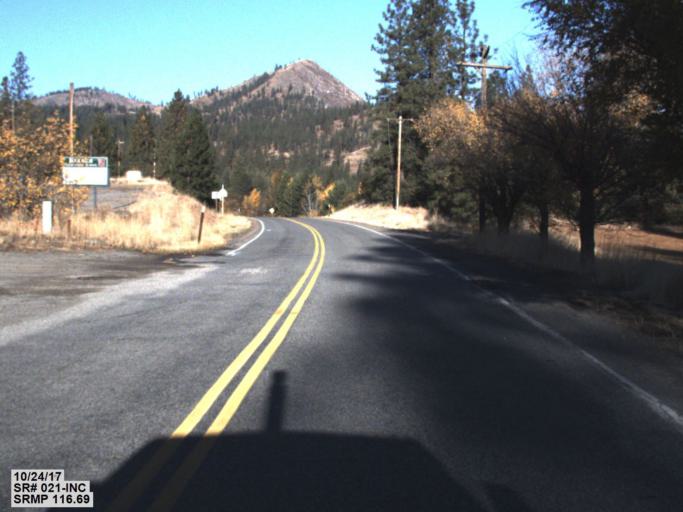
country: US
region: Washington
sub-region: Okanogan County
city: Coulee Dam
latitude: 48.0784
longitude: -118.6841
